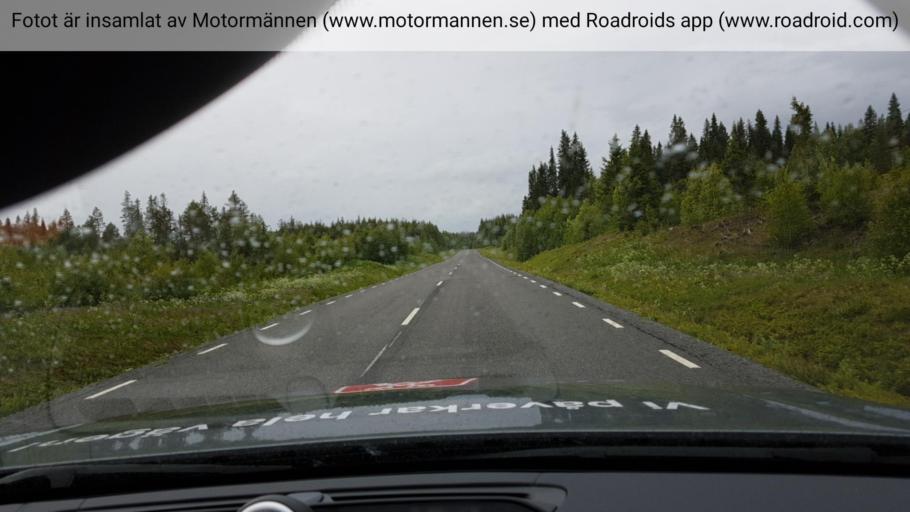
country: SE
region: Jaemtland
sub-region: Stroemsunds Kommun
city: Stroemsund
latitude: 63.6499
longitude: 15.1665
